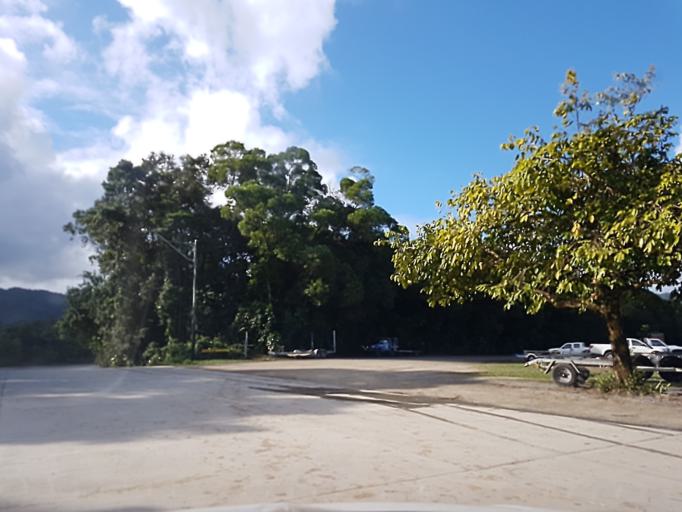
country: AU
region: Queensland
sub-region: Cairns
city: Port Douglas
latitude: -16.2620
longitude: 145.3933
